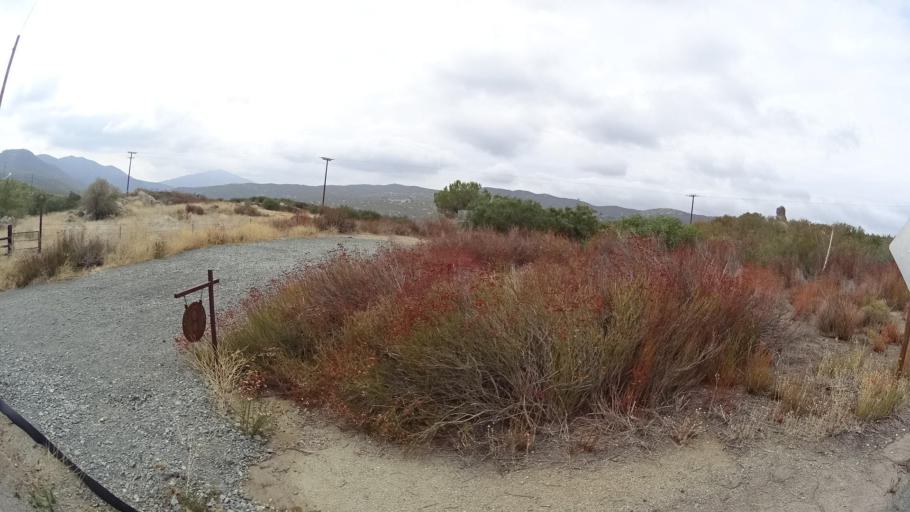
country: US
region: California
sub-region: San Diego County
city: Descanso
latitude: 32.9034
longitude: -116.6438
